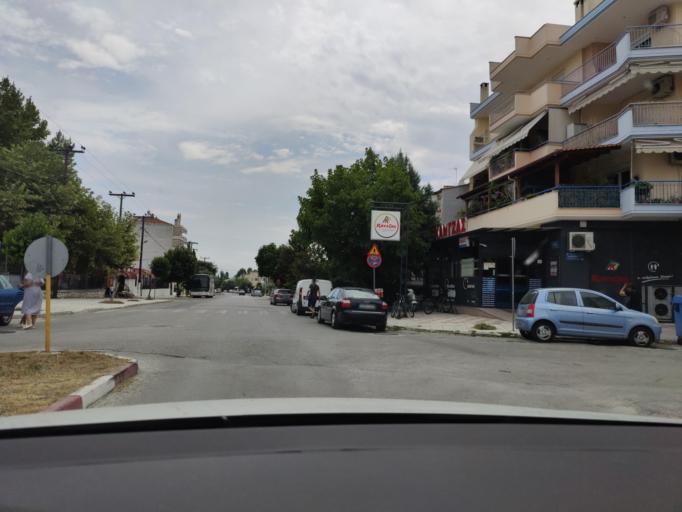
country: GR
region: Central Macedonia
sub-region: Nomos Serron
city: Serres
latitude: 41.0825
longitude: 23.5352
